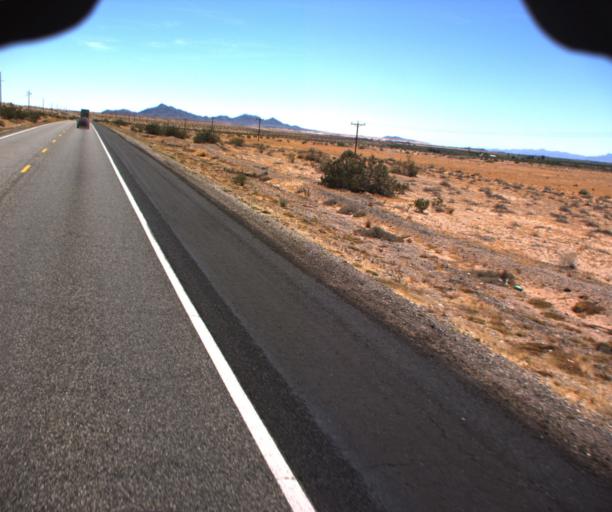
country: US
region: Arizona
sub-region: La Paz County
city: Parker
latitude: 34.1065
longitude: -114.2778
